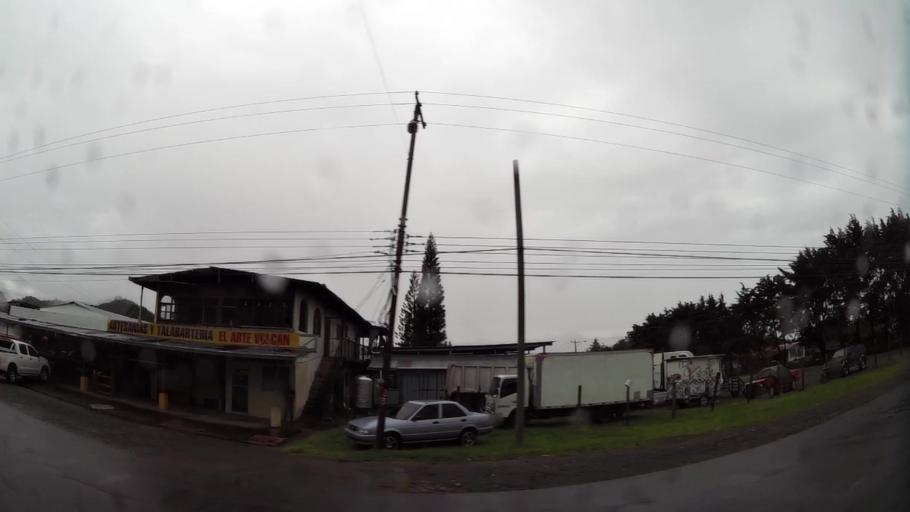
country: PA
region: Chiriqui
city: Volcan
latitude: 8.7699
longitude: -82.6345
